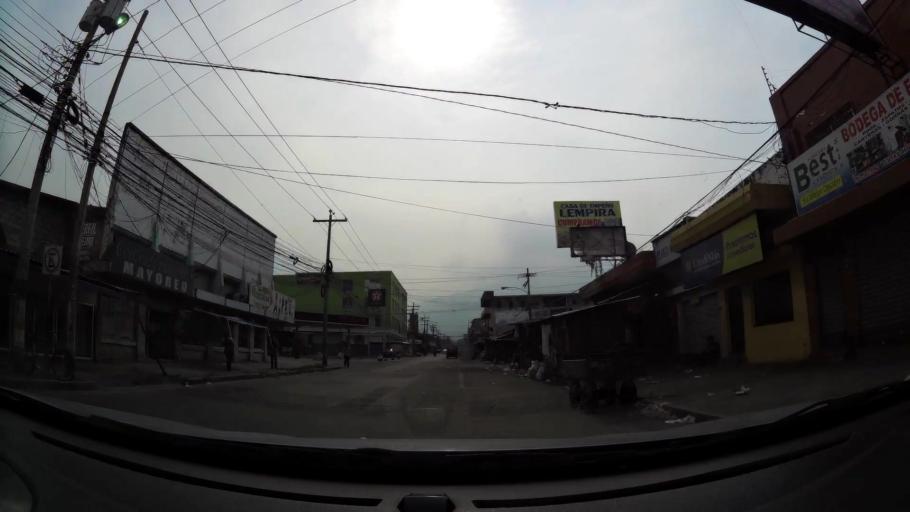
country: HN
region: Cortes
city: San Pedro Sula
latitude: 15.4995
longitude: -88.0176
